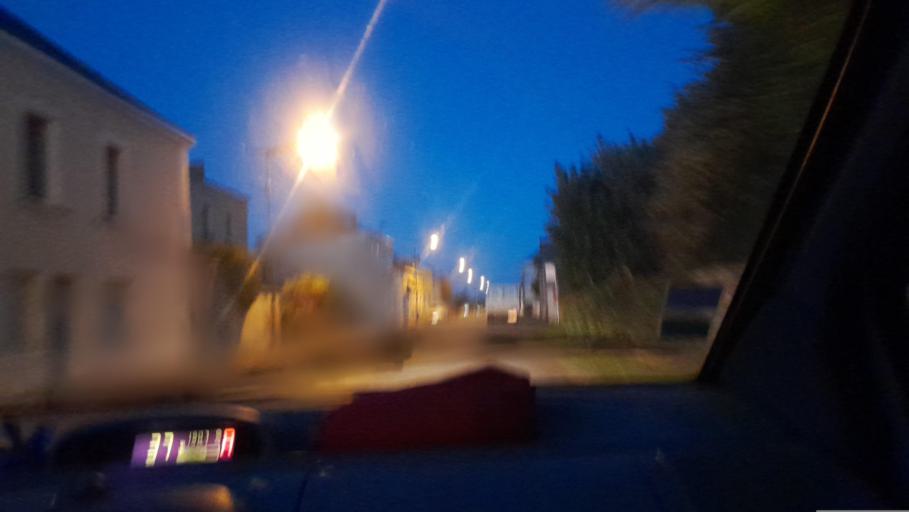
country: FR
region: Pays de la Loire
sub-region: Departement de la Mayenne
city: Ballots
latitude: 47.9422
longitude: -1.0840
